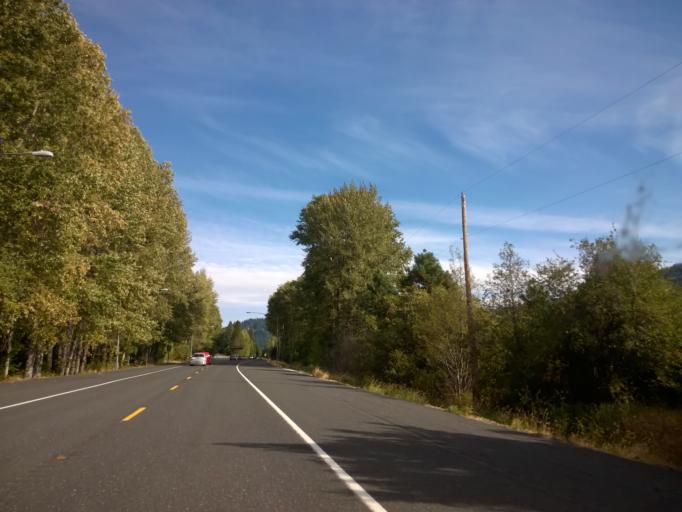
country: US
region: Washington
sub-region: Chelan County
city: Leavenworth
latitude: 47.7790
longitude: -120.8288
